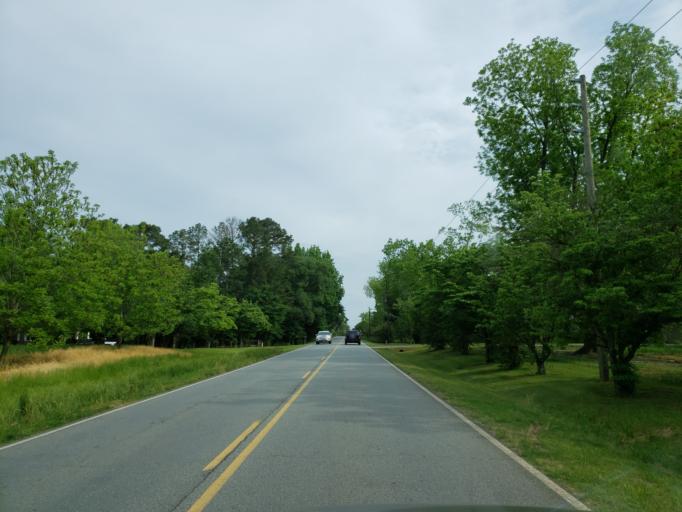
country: US
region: Georgia
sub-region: Dooly County
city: Vienna
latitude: 32.1535
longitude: -83.8809
